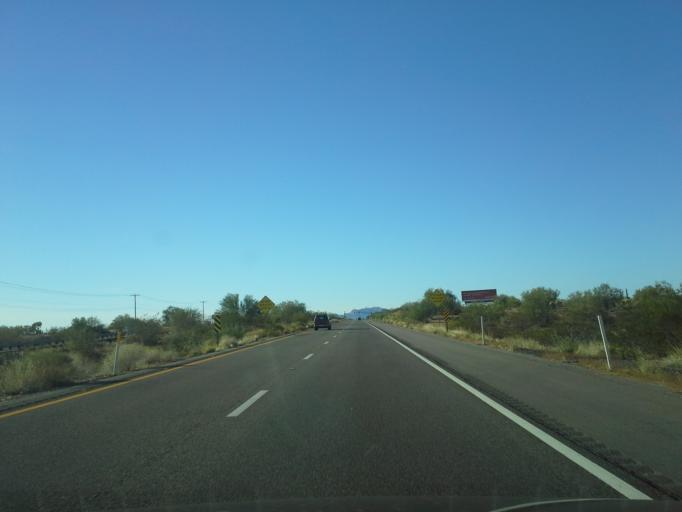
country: US
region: Arizona
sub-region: Pinal County
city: Gold Camp
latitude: 33.3323
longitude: -111.4362
